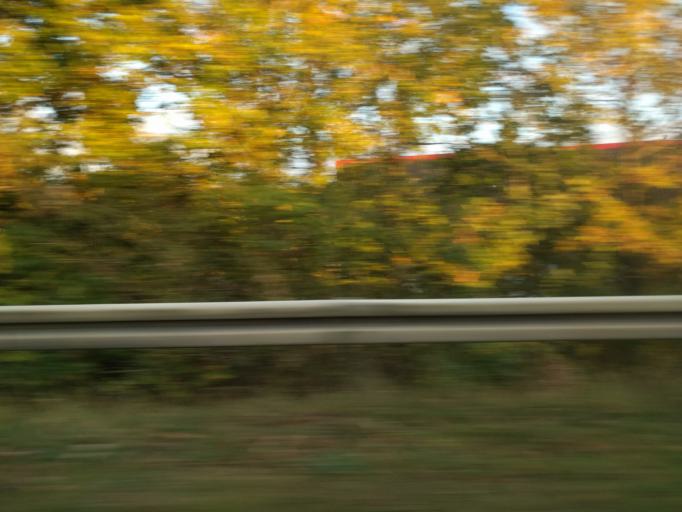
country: DK
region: South Denmark
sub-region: Kerteminde Kommune
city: Langeskov
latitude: 55.3568
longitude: 10.6070
